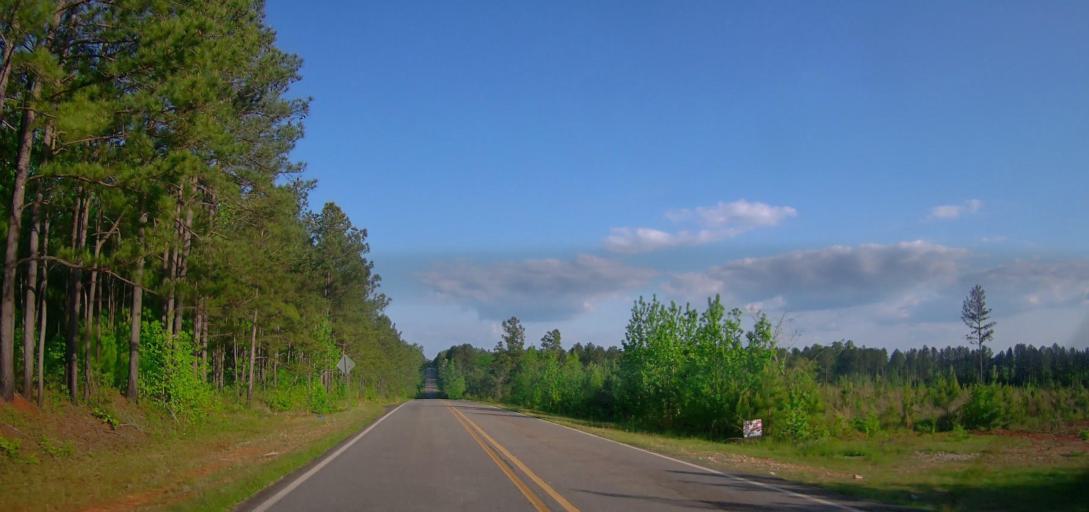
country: US
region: Georgia
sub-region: Putnam County
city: Eatonton
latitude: 33.2810
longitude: -83.3156
